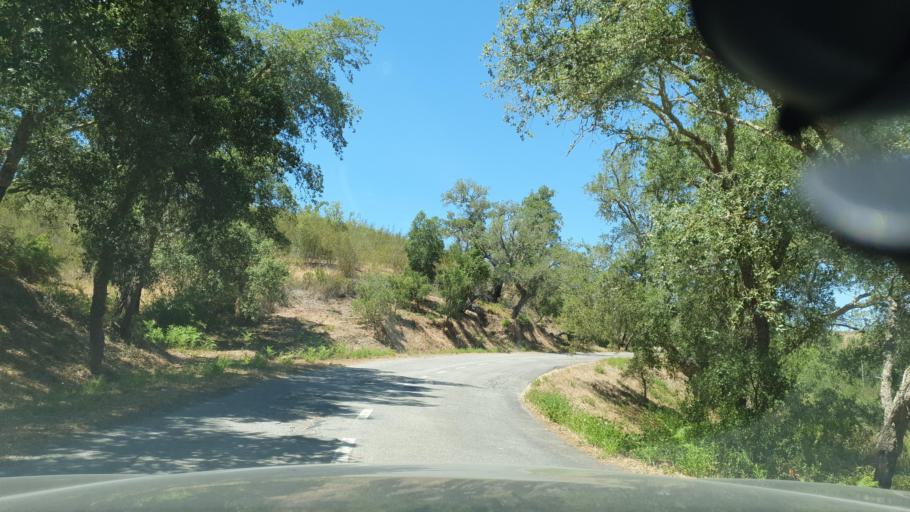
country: PT
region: Beja
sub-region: Odemira
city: Odemira
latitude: 37.6031
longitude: -8.4944
